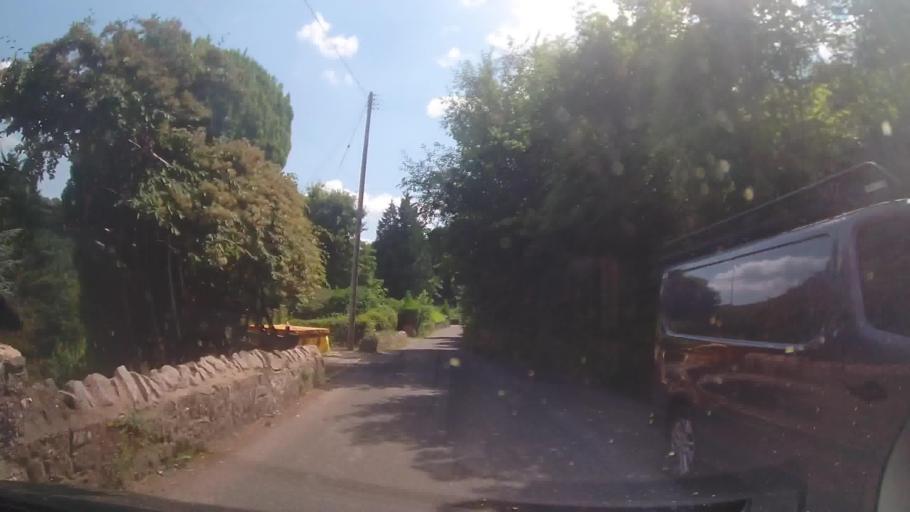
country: GB
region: England
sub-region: Herefordshire
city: Whitchurch
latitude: 51.8486
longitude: -2.6476
